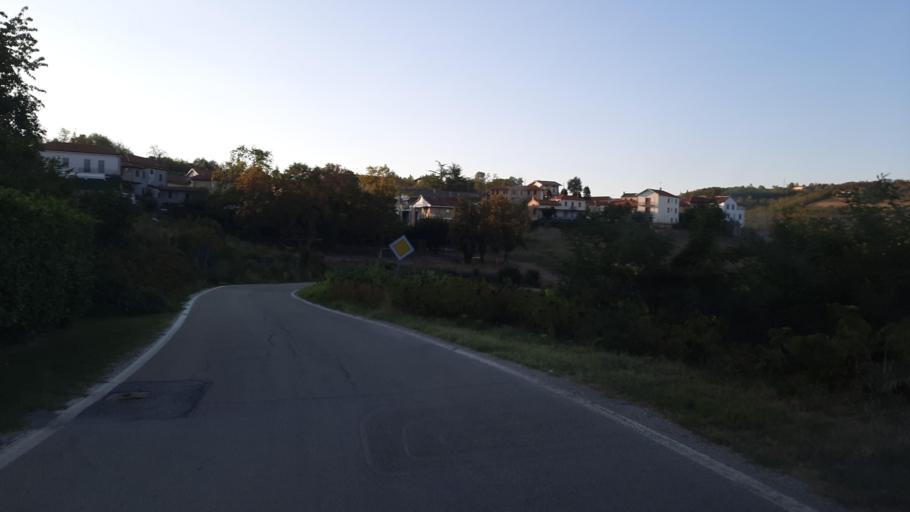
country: IT
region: Piedmont
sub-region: Provincia di Asti
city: Grazzano Badoglio
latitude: 45.0408
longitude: 8.3125
